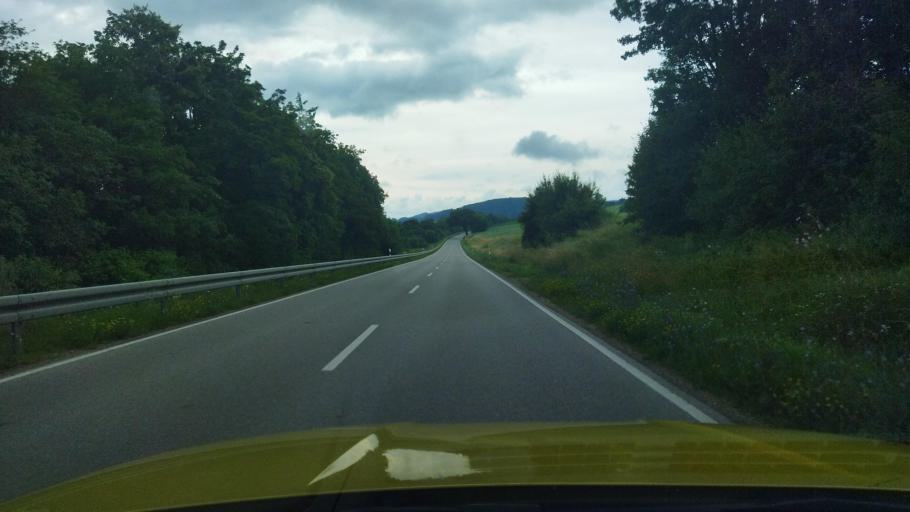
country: DE
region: Bavaria
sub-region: Regierungsbezirk Mittelfranken
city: Greding
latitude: 49.0680
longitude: 11.3112
